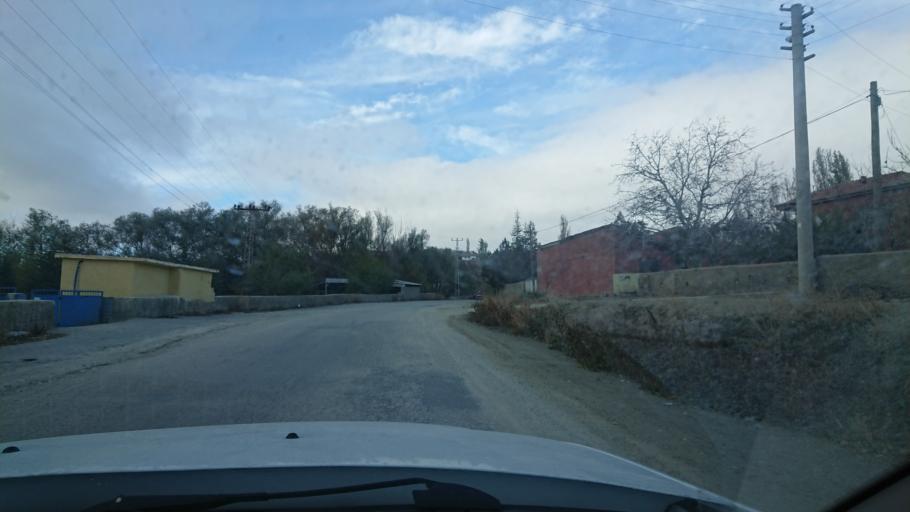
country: TR
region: Aksaray
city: Ortakoy
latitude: 38.7565
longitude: 34.0131
